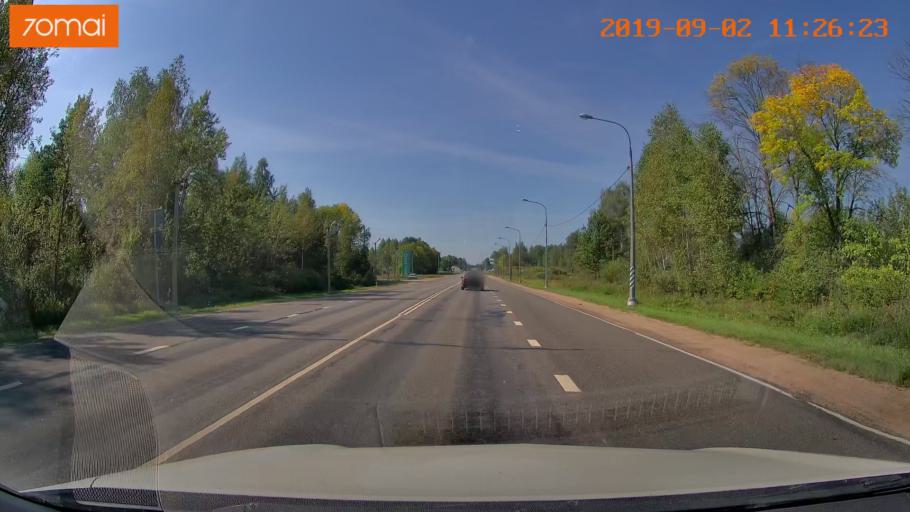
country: RU
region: Smolensk
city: Roslavl'
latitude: 53.9929
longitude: 32.9322
